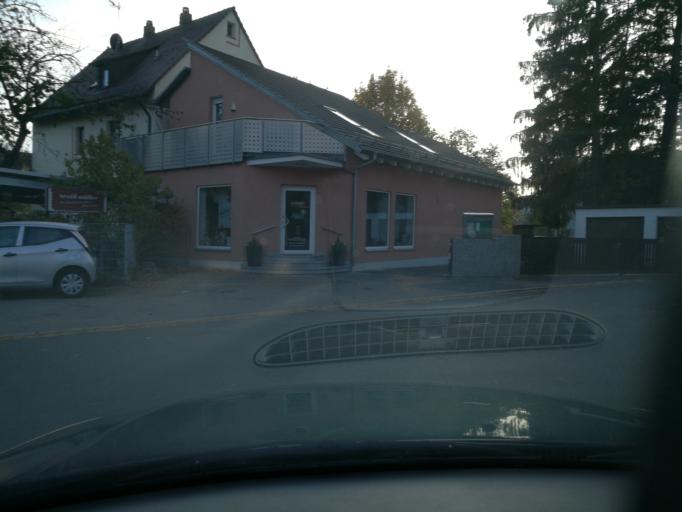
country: DE
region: Bavaria
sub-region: Regierungsbezirk Mittelfranken
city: Furth
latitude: 49.5102
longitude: 10.9778
